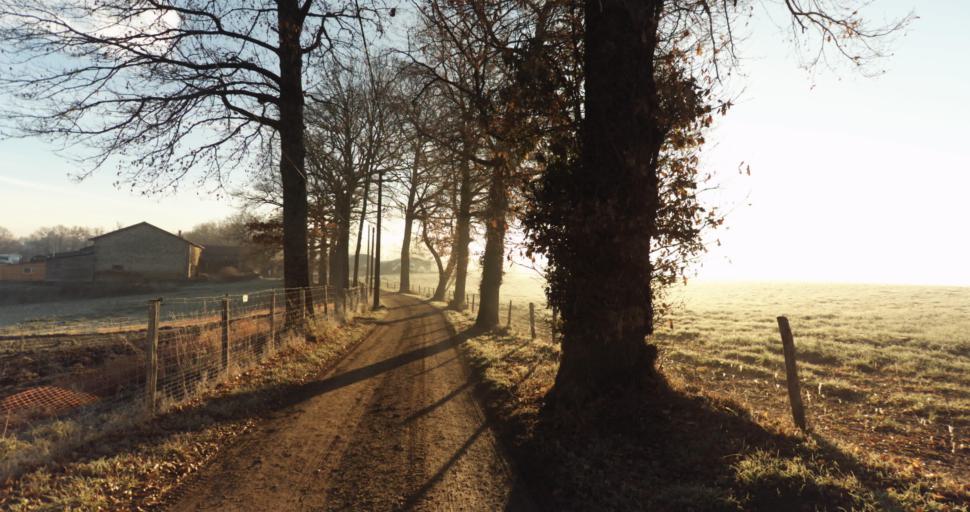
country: FR
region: Limousin
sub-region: Departement de la Haute-Vienne
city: Aixe-sur-Vienne
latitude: 45.7958
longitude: 1.1611
